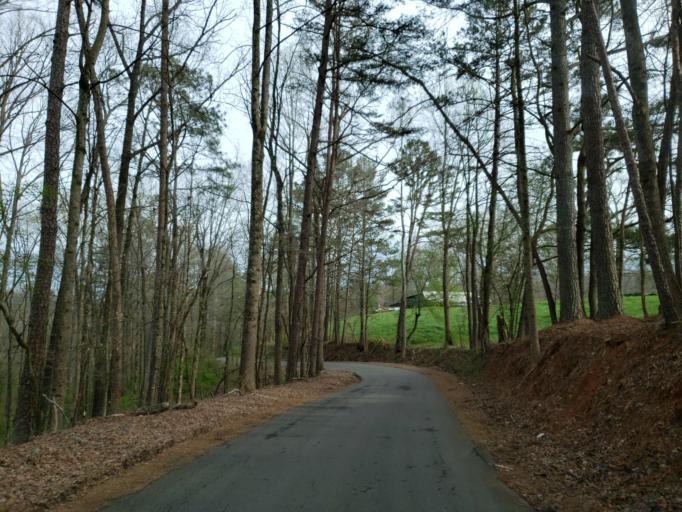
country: US
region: Georgia
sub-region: Pickens County
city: Nelson
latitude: 34.3849
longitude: -84.4289
